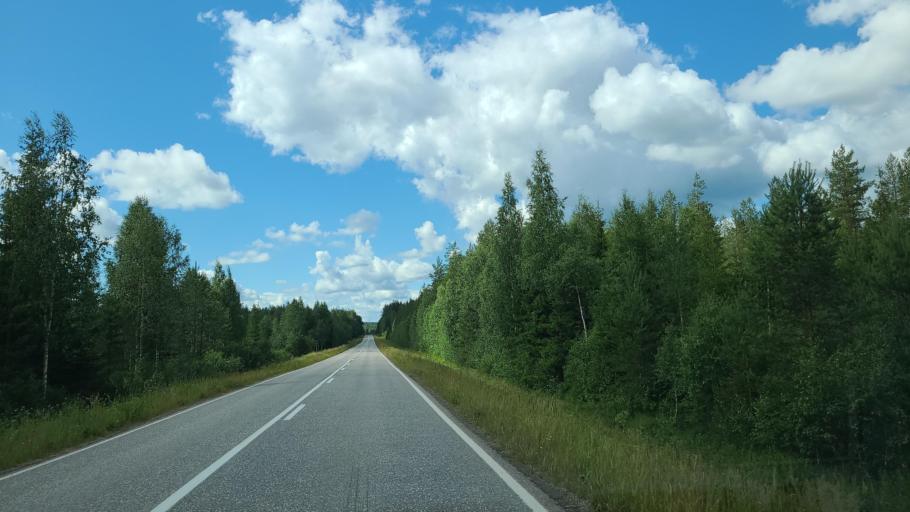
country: FI
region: Northern Savo
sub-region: Koillis-Savo
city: Kaavi
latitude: 62.9815
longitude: 28.8031
